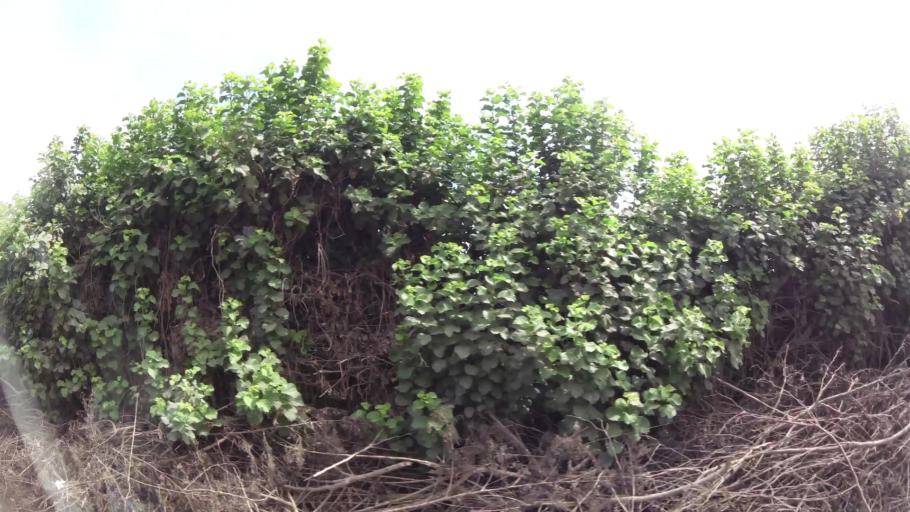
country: PE
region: Lima
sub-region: Provincia de Canete
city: Mala
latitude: -12.7291
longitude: -76.6202
